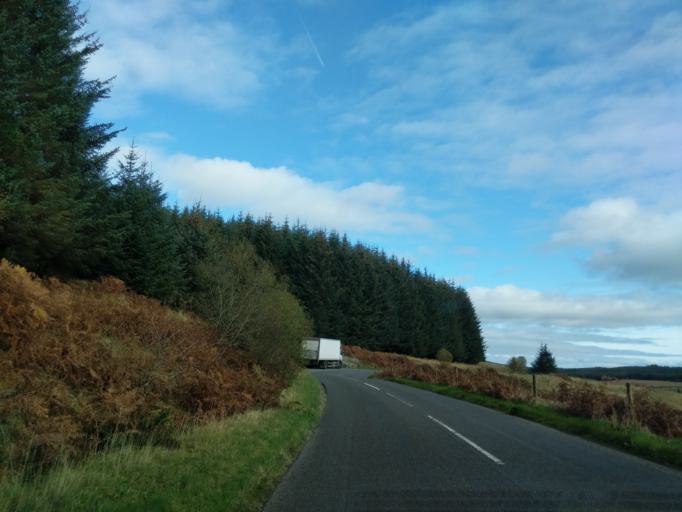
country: GB
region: Scotland
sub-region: Dumfries and Galloway
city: Castle Douglas
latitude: 55.1388
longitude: -4.0473
